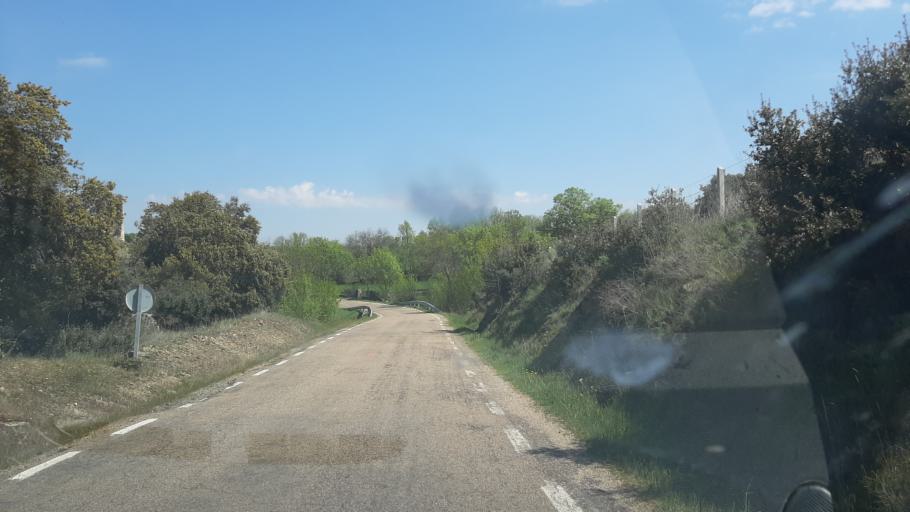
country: ES
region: Castille and Leon
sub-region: Provincia de Salamanca
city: Tejeda y Segoyuela
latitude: 40.6276
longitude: -6.0224
